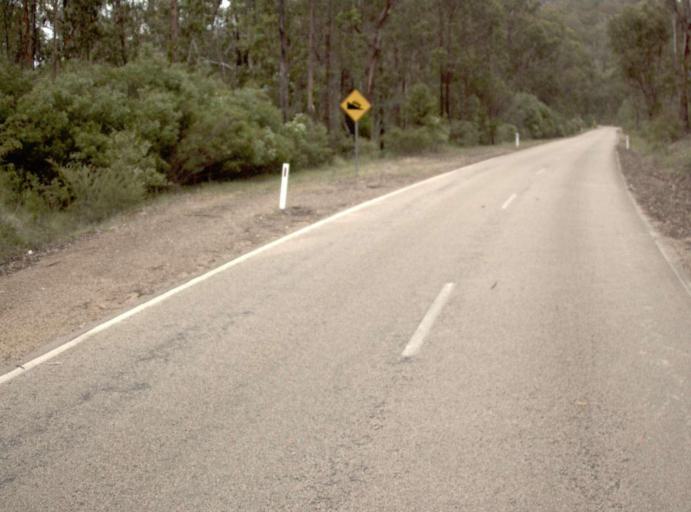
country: AU
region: Victoria
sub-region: East Gippsland
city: Bairnsdale
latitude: -37.6123
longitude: 147.1904
